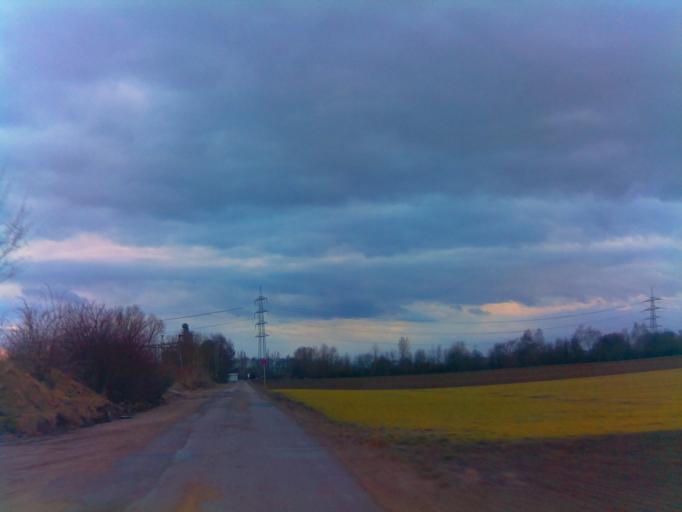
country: DE
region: Hesse
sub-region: Regierungsbezirk Darmstadt
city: Biblis
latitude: 49.7065
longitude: 8.4549
